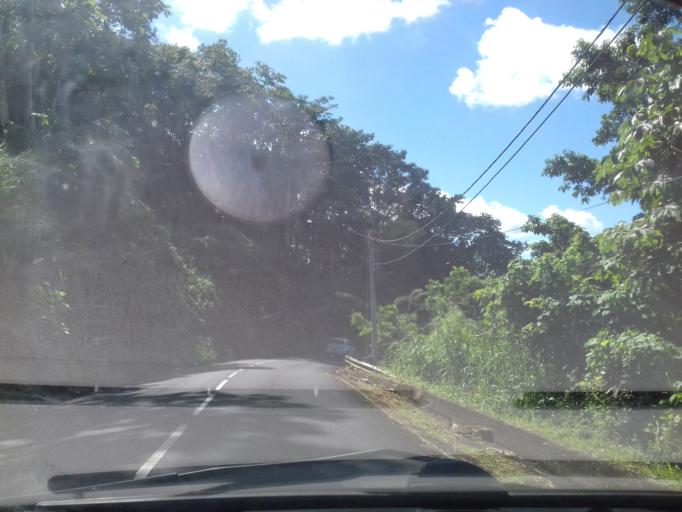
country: MQ
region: Martinique
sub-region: Martinique
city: Saint-Joseph
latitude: 14.6605
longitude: -61.0456
